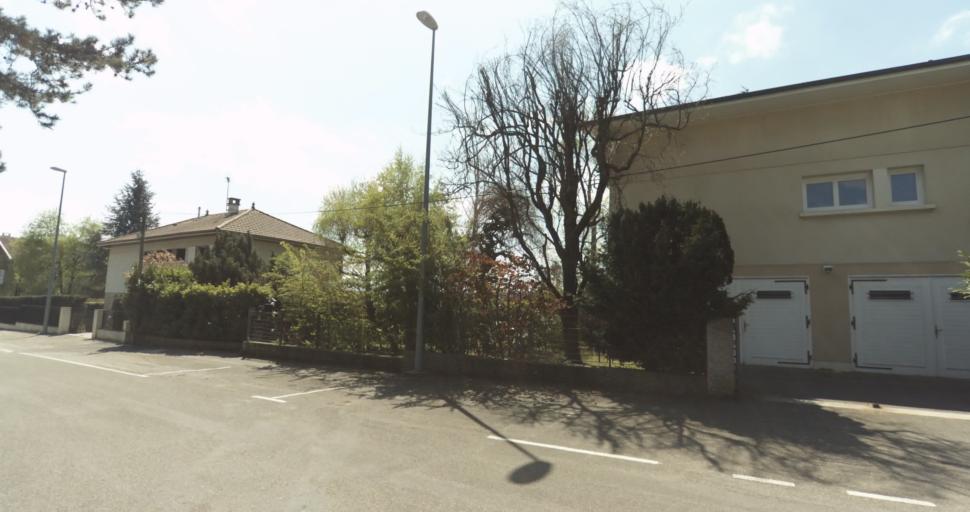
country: FR
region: Rhone-Alpes
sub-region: Departement de l'Isere
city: Saint-Marcellin
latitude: 45.1487
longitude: 5.3055
